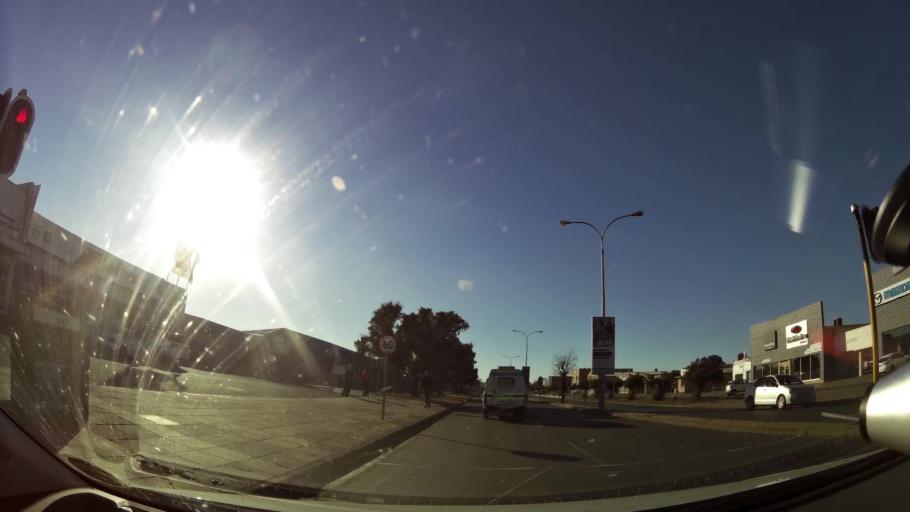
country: ZA
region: Northern Cape
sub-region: Frances Baard District Municipality
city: Kimberley
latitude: -28.7441
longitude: 24.7515
